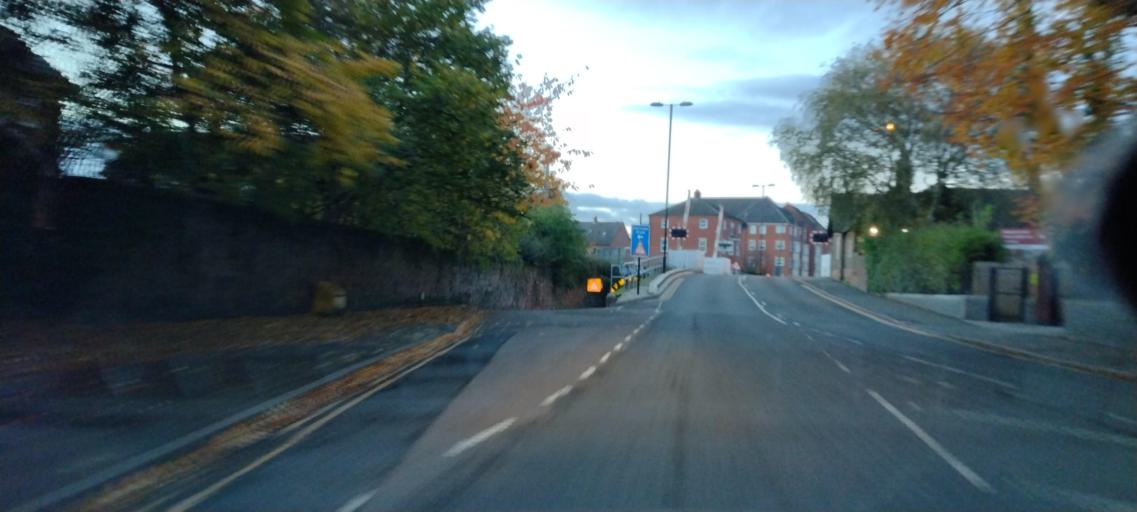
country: GB
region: England
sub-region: Coventry
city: Coventry
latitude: 52.4130
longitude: -1.5222
